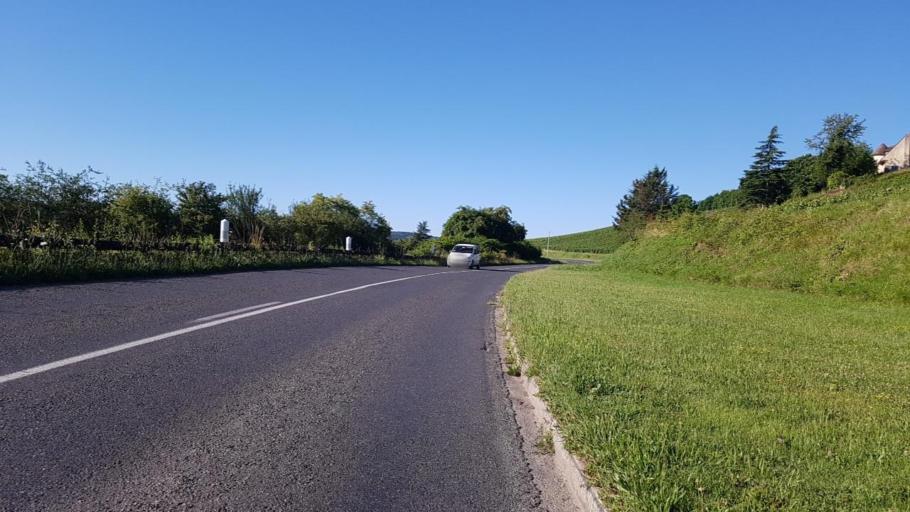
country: FR
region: Picardie
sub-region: Departement de l'Aisne
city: Essomes-sur-Marne
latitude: 49.0107
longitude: 3.3757
